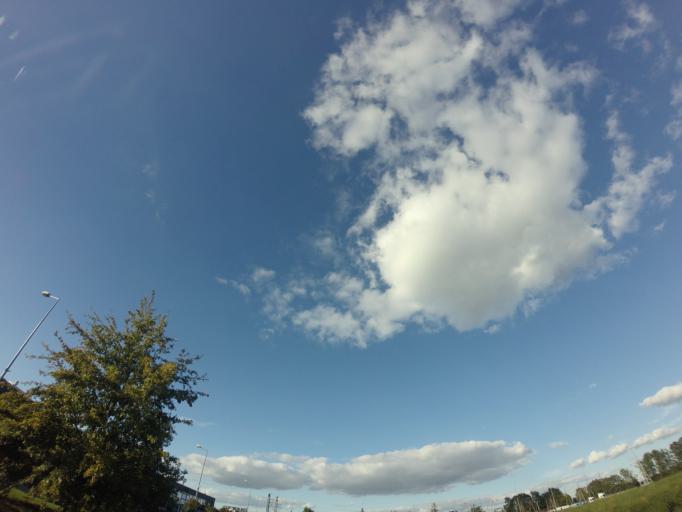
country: PL
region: Greater Poland Voivodeship
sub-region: Powiat nowotomyski
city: Nowy Tomysl
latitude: 52.2953
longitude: 16.1270
